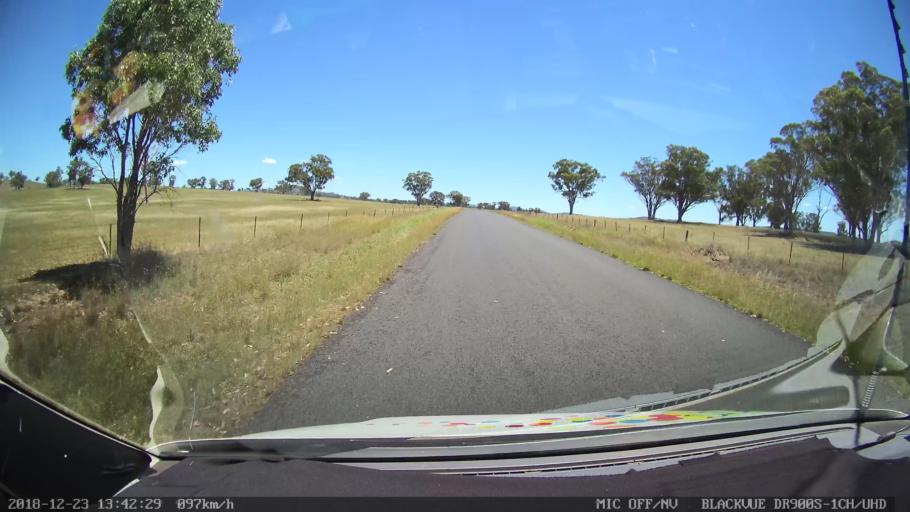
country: AU
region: New South Wales
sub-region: Armidale Dumaresq
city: Armidale
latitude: -30.4776
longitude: 151.1621
